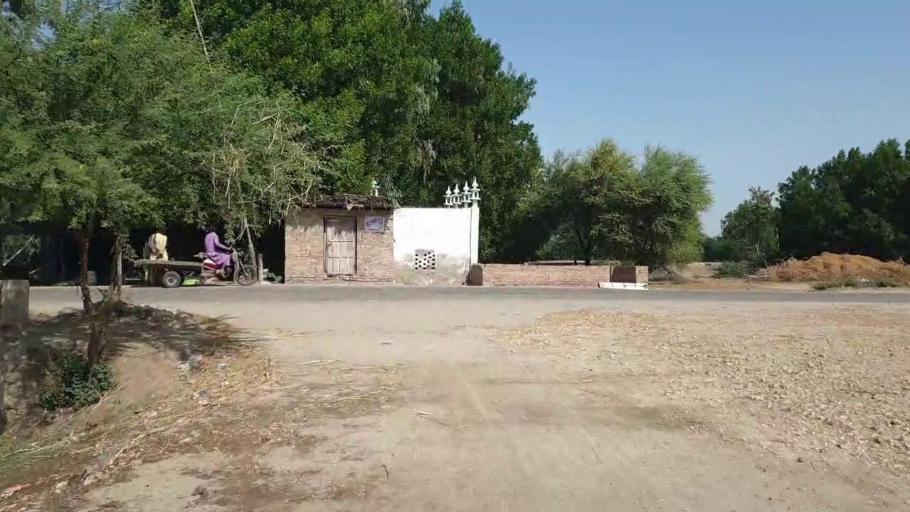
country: PK
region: Sindh
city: Tando Bago
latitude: 24.7675
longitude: 69.0232
